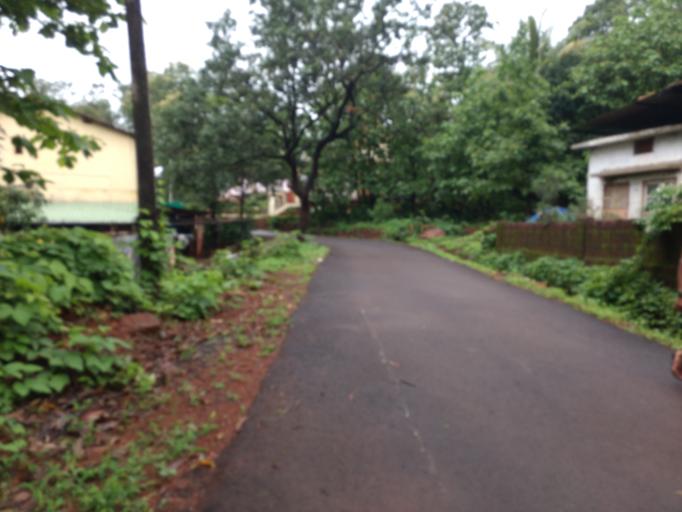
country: IN
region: Maharashtra
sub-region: Ratnagiri
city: Guhagar
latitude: 17.4946
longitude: 73.1891
